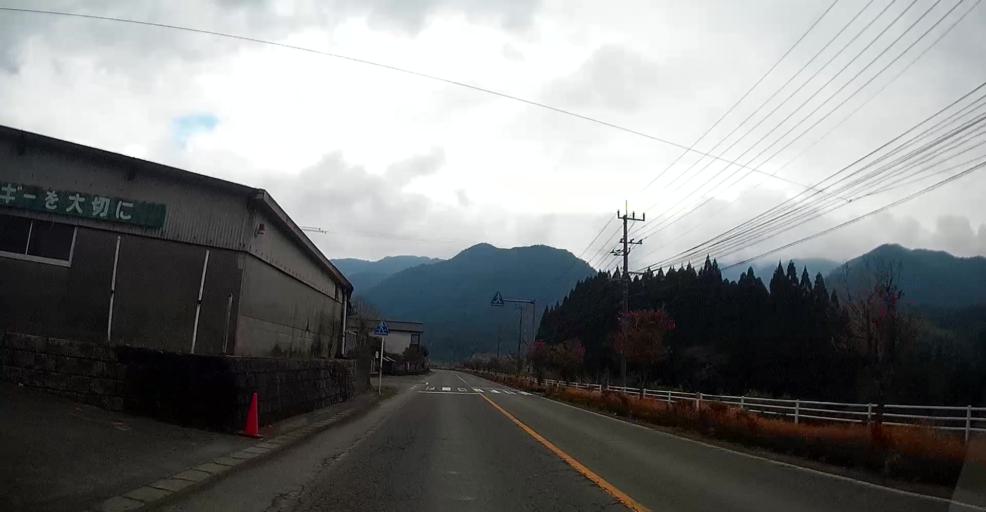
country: JP
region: Kumamoto
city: Matsubase
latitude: 32.6178
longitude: 130.8370
